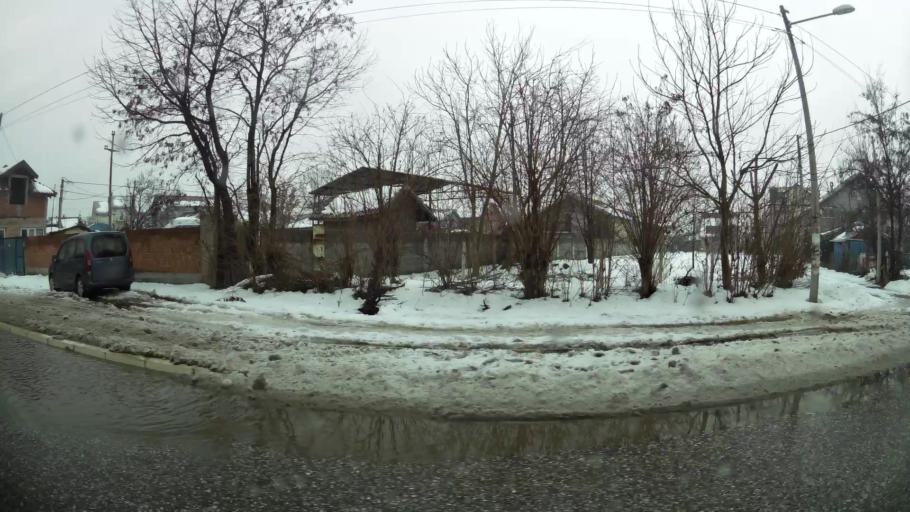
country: RS
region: Central Serbia
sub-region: Belgrade
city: Zemun
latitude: 44.8563
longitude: 20.3582
